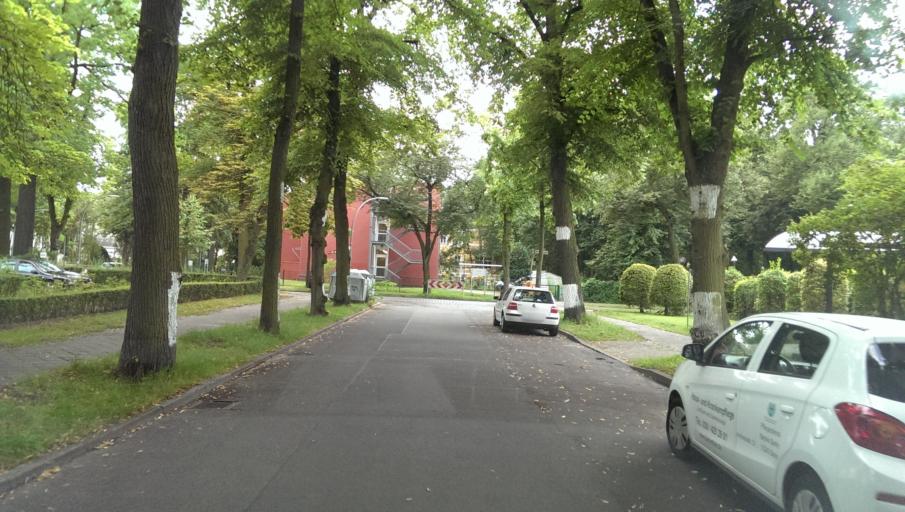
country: DE
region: Berlin
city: Lankwitz
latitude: 52.4334
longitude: 13.3295
